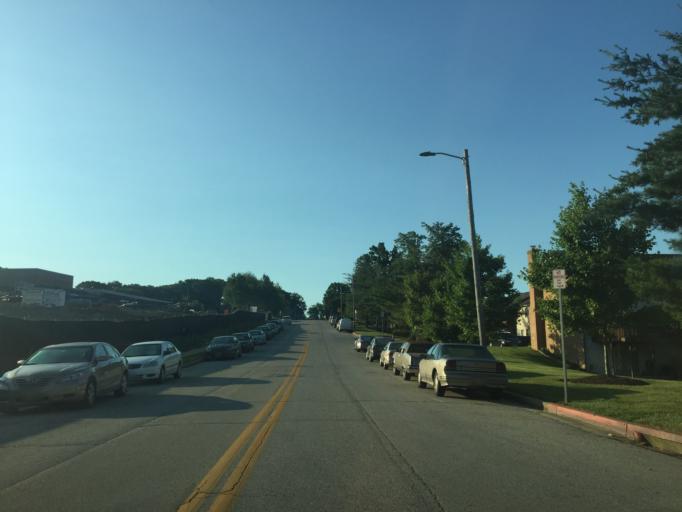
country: US
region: Maryland
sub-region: Howard County
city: Elkridge
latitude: 39.2319
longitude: -76.7023
